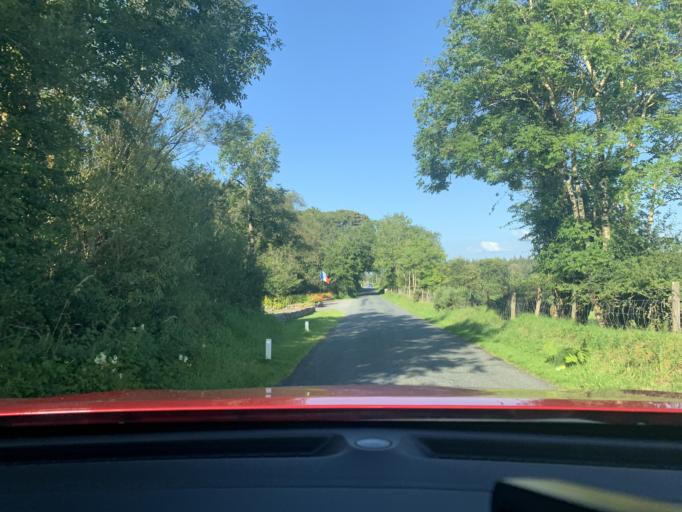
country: IE
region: Connaught
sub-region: Sligo
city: Tobercurry
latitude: 54.1239
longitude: -8.7416
